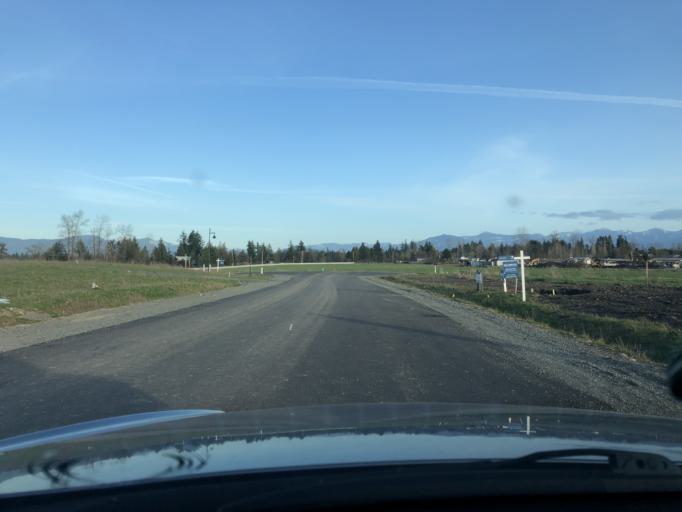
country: US
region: Washington
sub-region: Pierce County
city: Prairie Ridge
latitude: 47.1936
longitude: -122.1136
